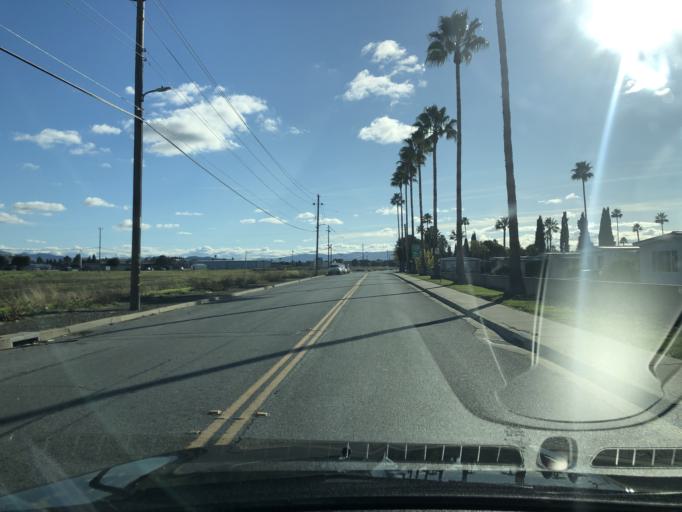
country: US
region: California
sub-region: Contra Costa County
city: Pacheco
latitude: 37.9890
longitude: -122.0630
